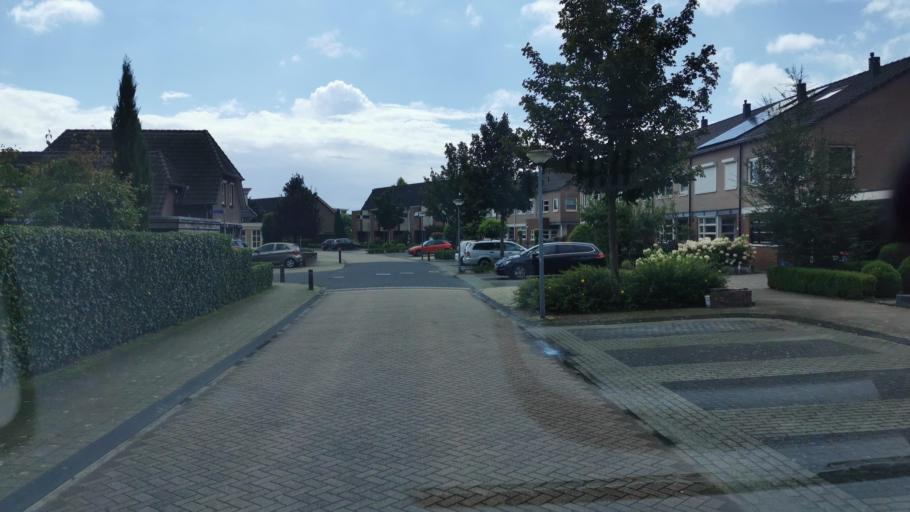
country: NL
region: Overijssel
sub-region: Gemeente Losser
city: Losser
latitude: 52.2735
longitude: 7.0003
